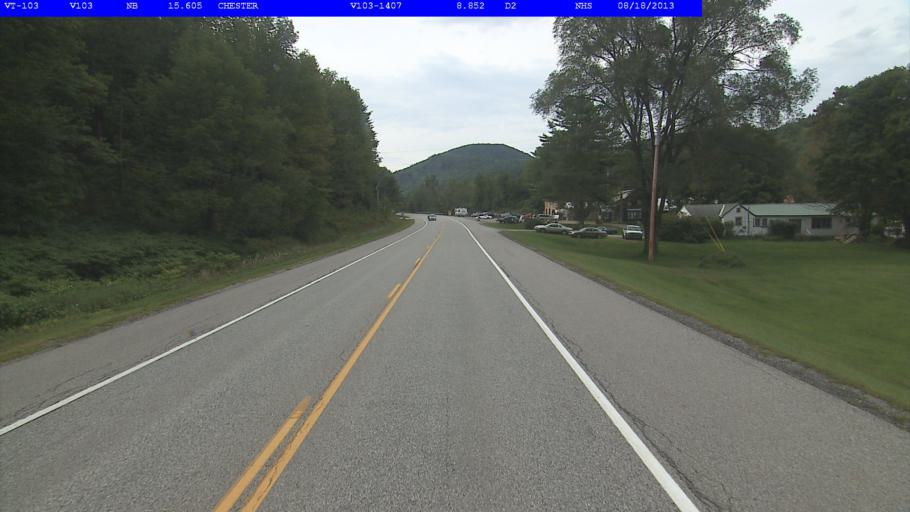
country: US
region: Vermont
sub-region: Windsor County
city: Chester
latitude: 43.3381
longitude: -72.6178
